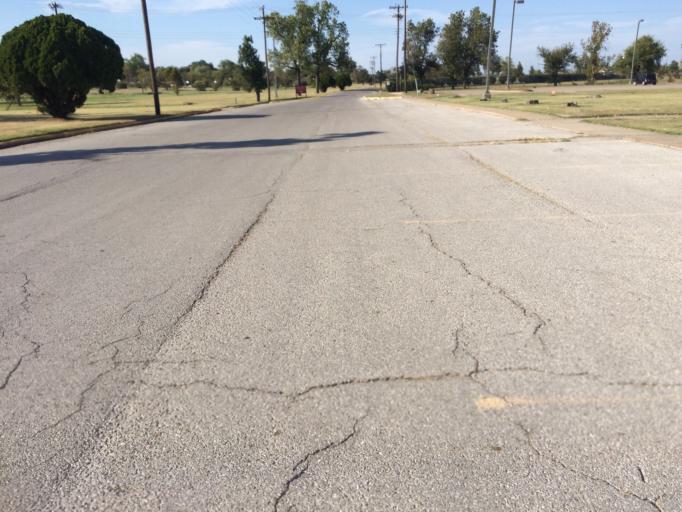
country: US
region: Oklahoma
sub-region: Cleveland County
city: Norman
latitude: 35.2269
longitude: -97.4299
